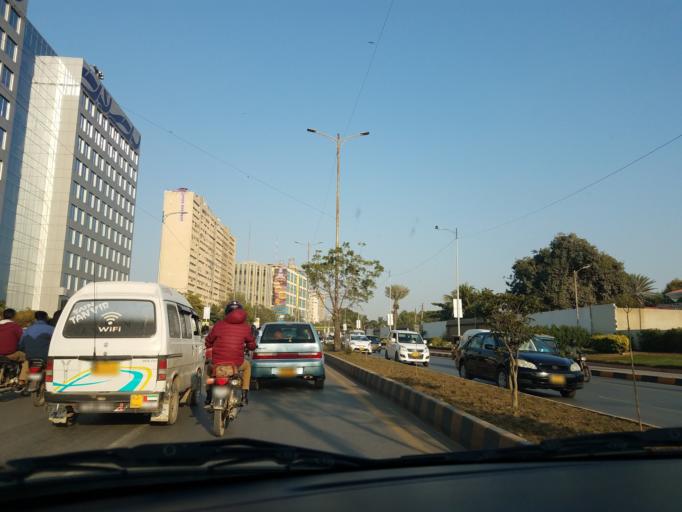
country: PK
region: Sindh
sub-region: Karachi District
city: Karachi
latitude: 24.8564
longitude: 67.0416
